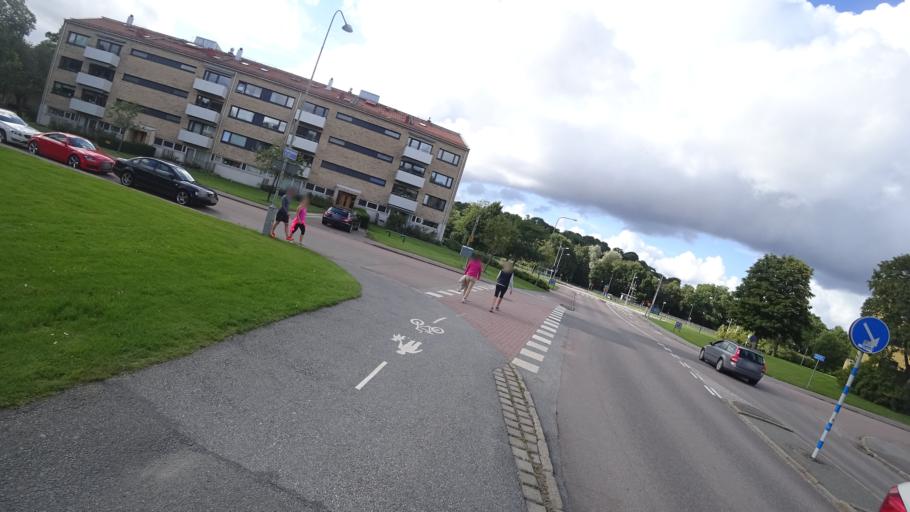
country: SE
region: Vaestra Goetaland
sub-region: Molndal
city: Moelndal
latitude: 57.7014
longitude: 12.0232
